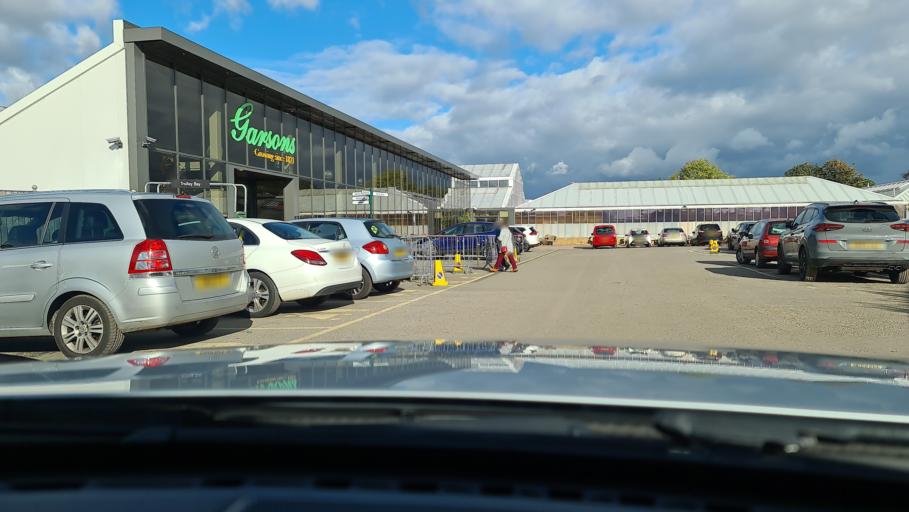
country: GB
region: England
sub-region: Surrey
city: Esher
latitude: 51.3629
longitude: -0.3868
